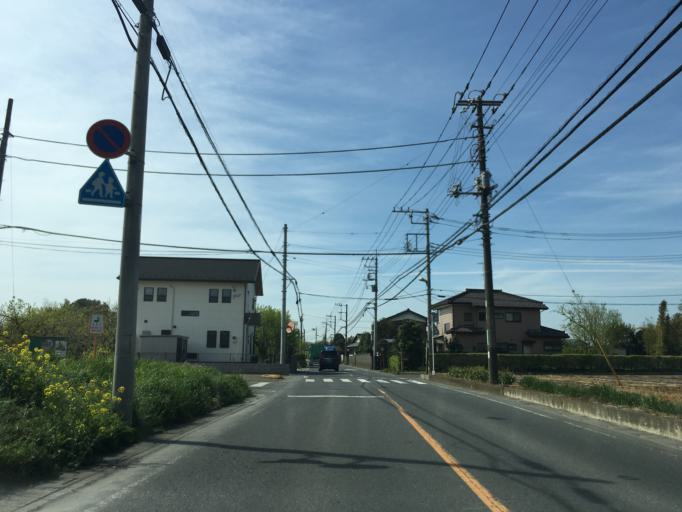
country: JP
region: Saitama
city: Ageoshimo
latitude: 35.9786
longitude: 139.6333
